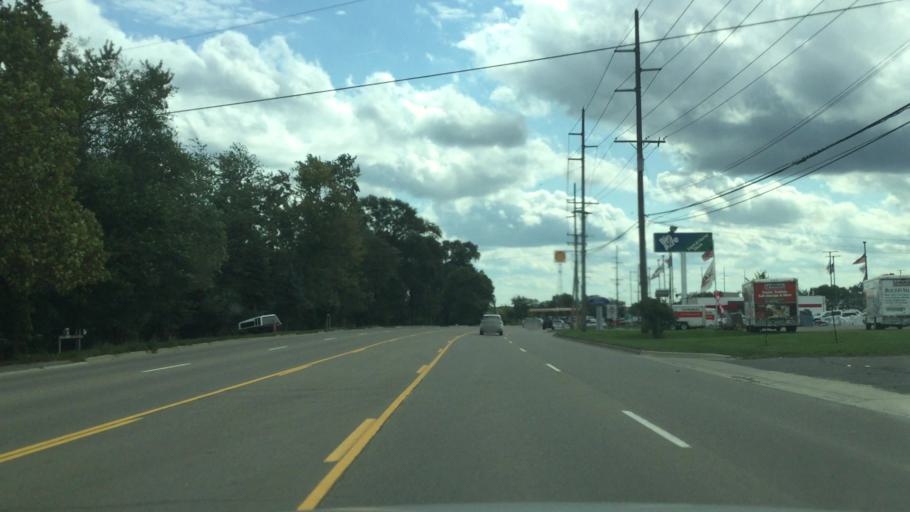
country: US
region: Michigan
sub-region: Livingston County
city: Brighton
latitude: 42.5531
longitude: -83.7906
